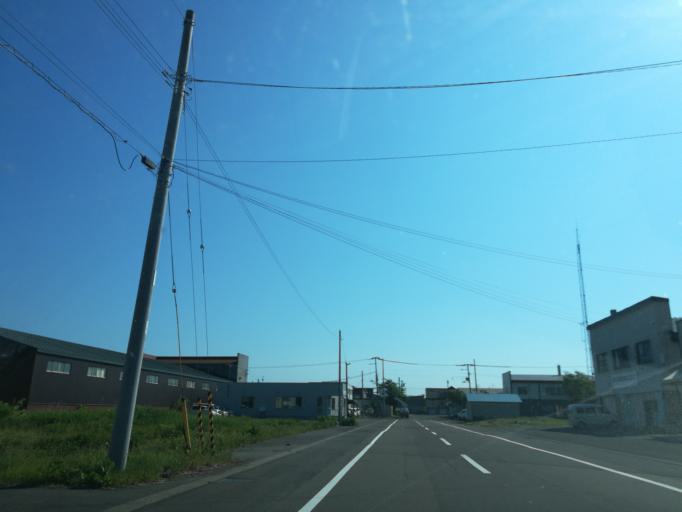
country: JP
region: Hokkaido
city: Iwamizawa
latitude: 43.1887
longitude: 141.7444
